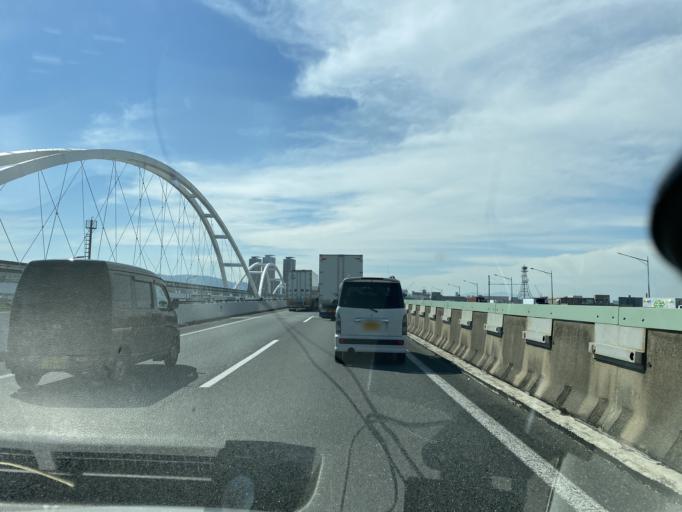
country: JP
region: Osaka
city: Kadoma
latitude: 34.7598
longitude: 135.5723
